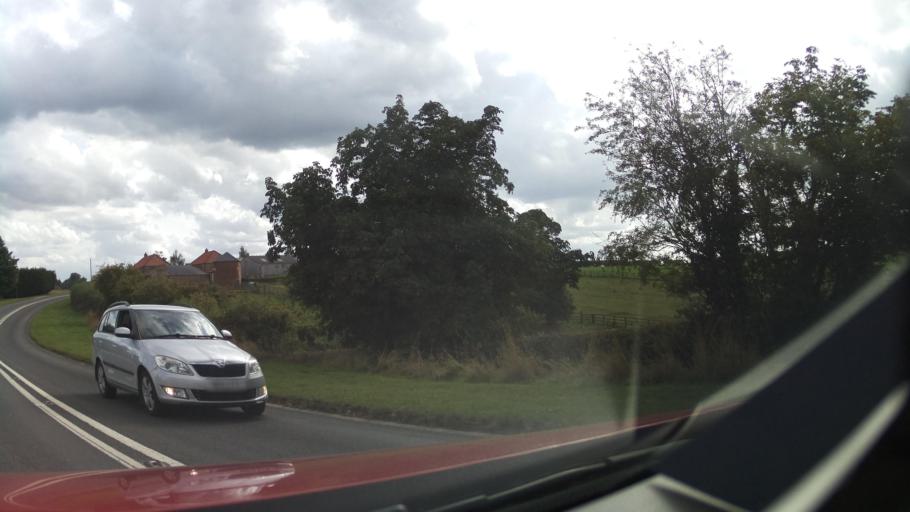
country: GB
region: England
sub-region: North Yorkshire
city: Ripon
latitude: 54.1604
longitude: -1.5421
